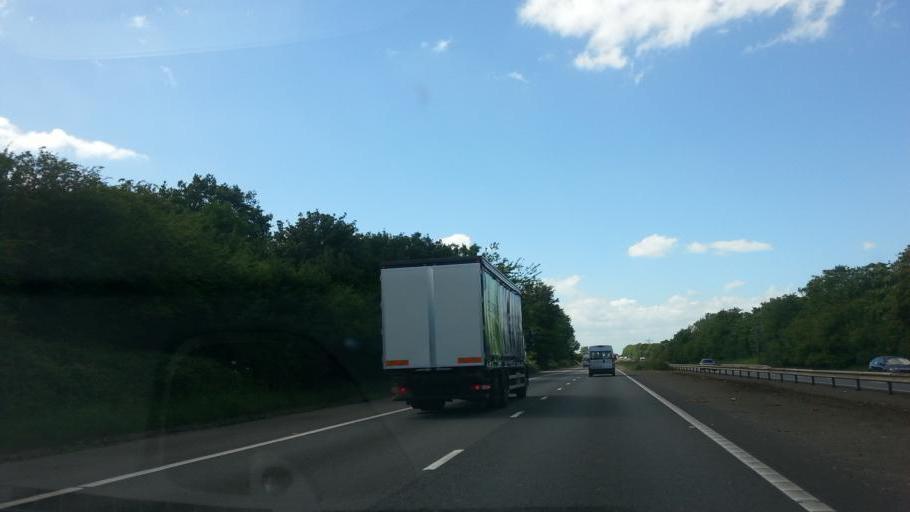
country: GB
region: England
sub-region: Hertfordshire
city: Stevenage
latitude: 51.8961
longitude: -0.2146
